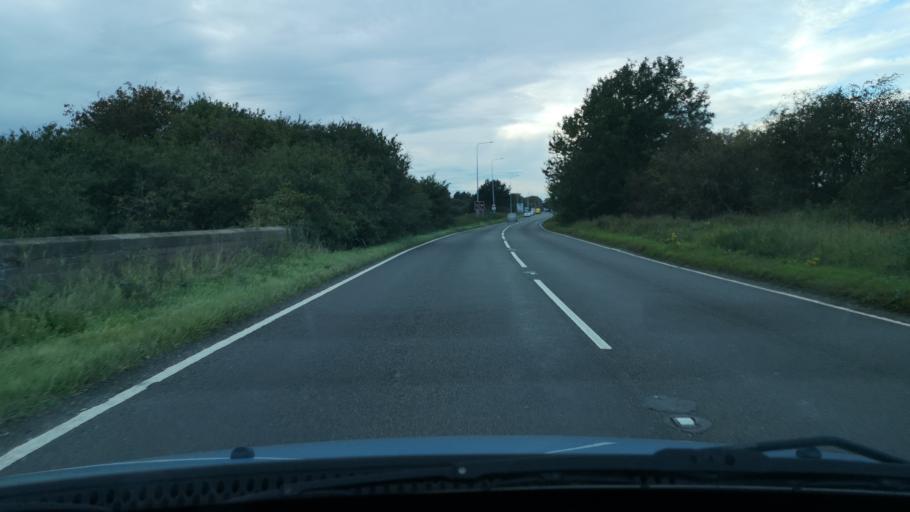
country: GB
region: England
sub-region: North Lincolnshire
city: Crowle
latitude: 53.5834
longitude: -0.8107
